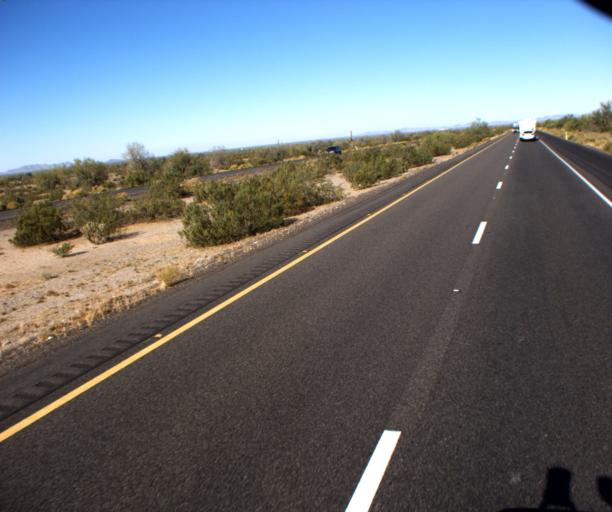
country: US
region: Arizona
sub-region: Maricopa County
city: Gila Bend
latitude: 32.9112
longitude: -112.6064
